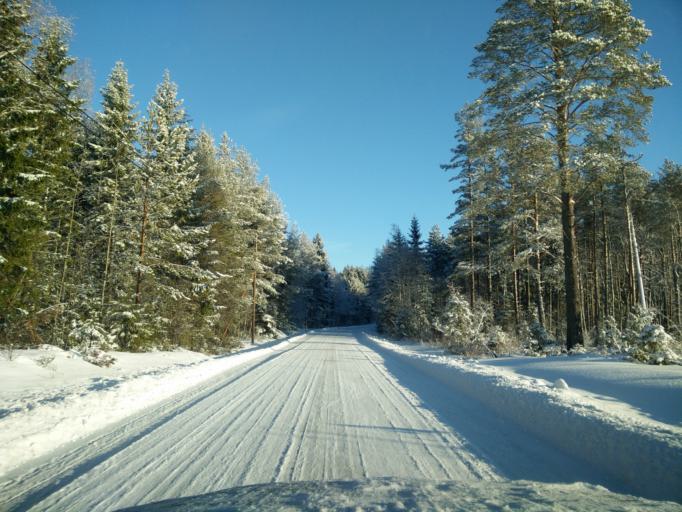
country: SE
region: Vaesternorrland
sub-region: Sundsvalls Kommun
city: Njurundabommen
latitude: 62.2365
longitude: 17.5762
